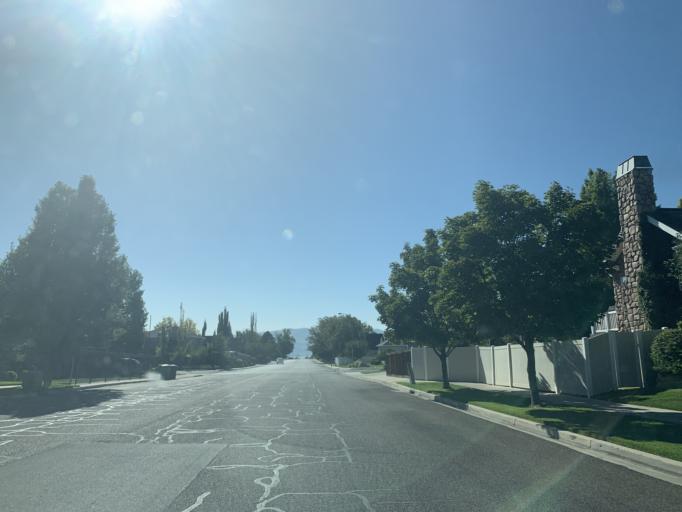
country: US
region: Utah
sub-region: Utah County
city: Orem
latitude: 40.2571
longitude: -111.6910
